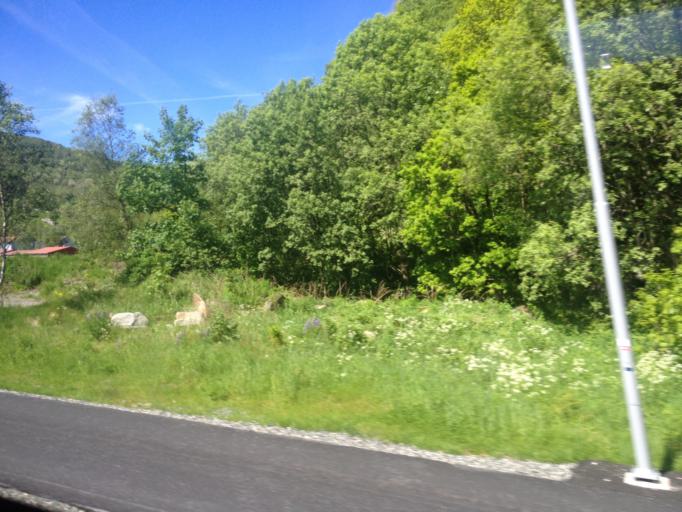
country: NO
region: Rogaland
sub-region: Bjerkreim
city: Vikesa
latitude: 58.5313
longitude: 6.1373
